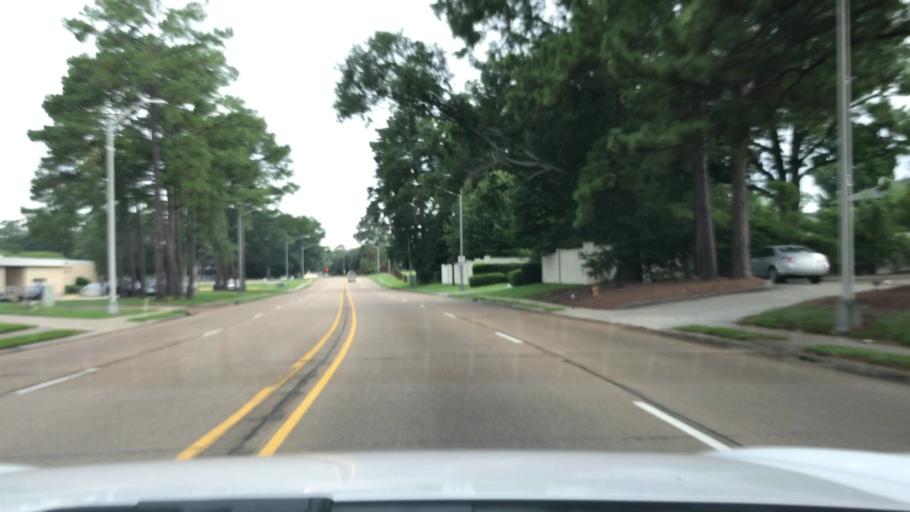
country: US
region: Louisiana
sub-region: East Baton Rouge Parish
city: Baton Rouge
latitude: 30.4387
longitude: -91.1331
